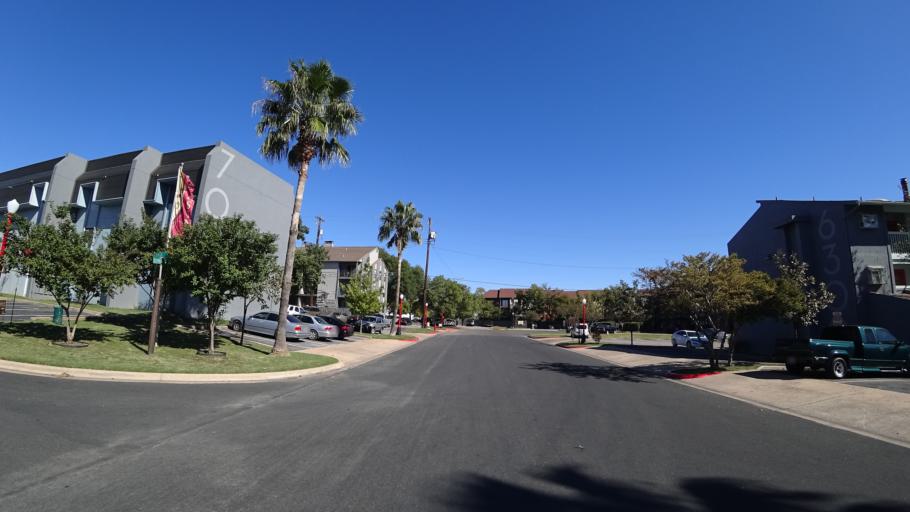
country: US
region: Texas
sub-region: Travis County
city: Austin
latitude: 30.3310
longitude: -97.7214
